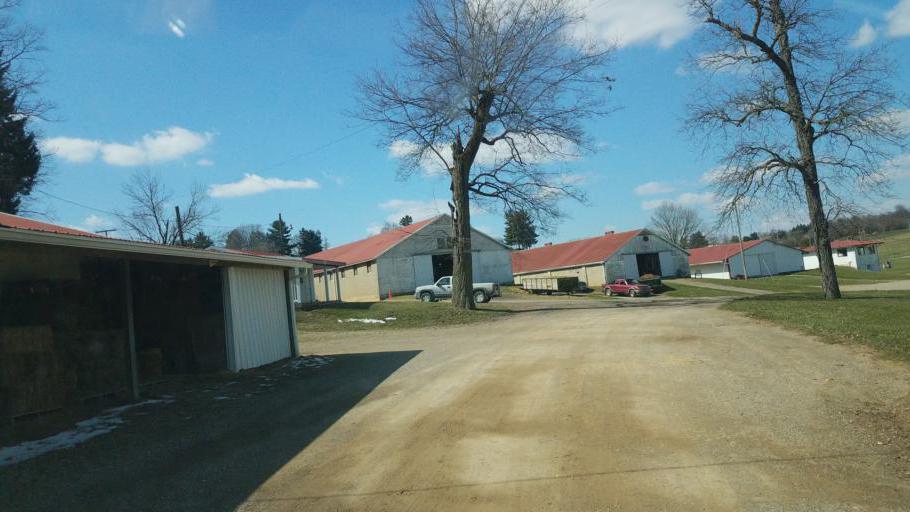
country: US
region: Ohio
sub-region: Knox County
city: Mount Vernon
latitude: 40.4150
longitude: -82.4749
